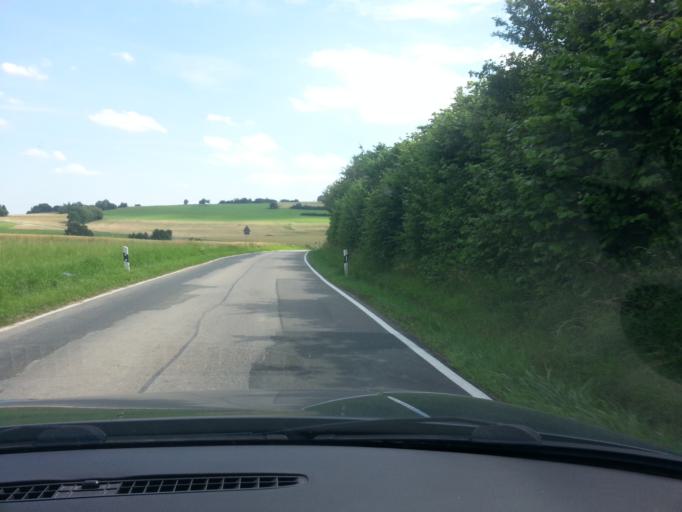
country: DE
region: Saarland
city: Blieskastel
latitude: 49.1991
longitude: 7.2829
